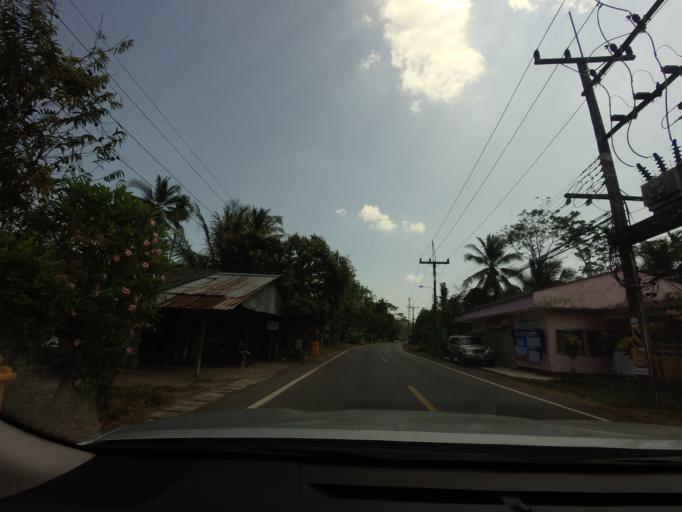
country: TH
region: Phangnga
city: Takua Thung
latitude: 8.2495
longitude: 98.3889
